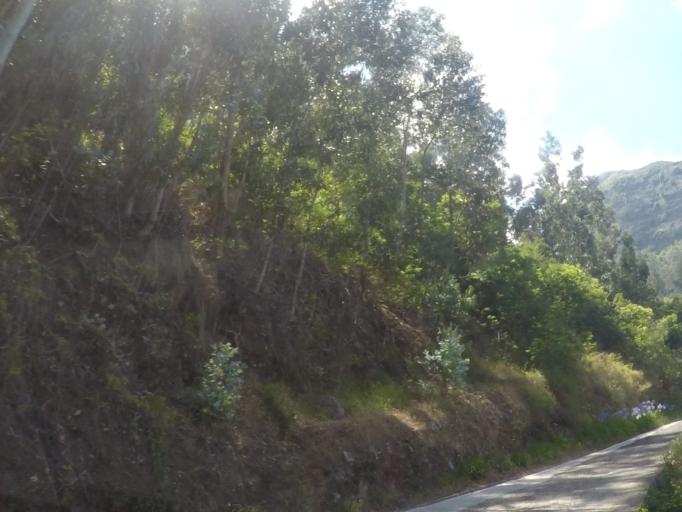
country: PT
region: Madeira
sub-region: Camara de Lobos
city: Curral das Freiras
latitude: 32.7141
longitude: -16.9732
